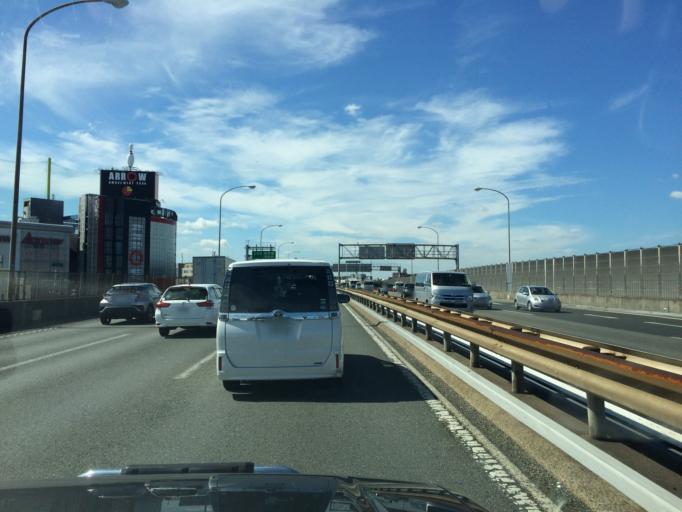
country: JP
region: Osaka
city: Matsubara
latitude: 34.5863
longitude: 135.5723
